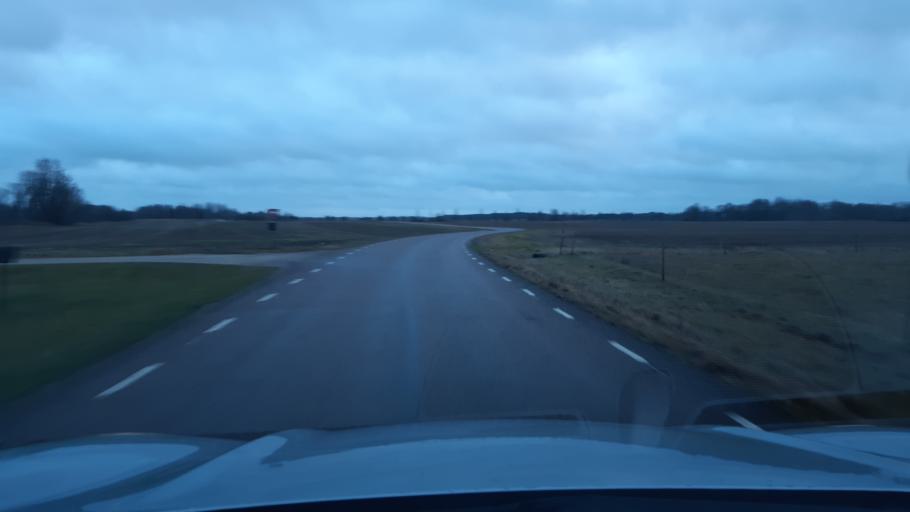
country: EE
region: Raplamaa
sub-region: Rapla vald
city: Rapla
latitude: 59.0129
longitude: 24.7049
